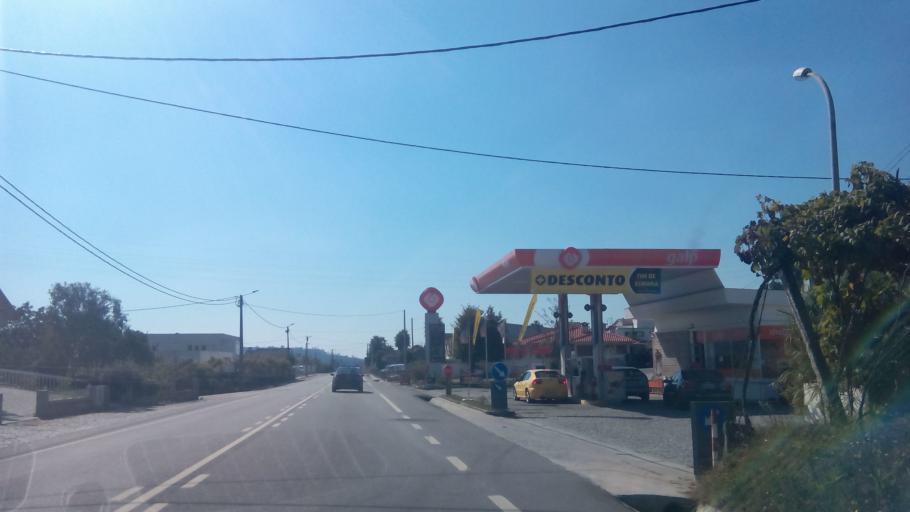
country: PT
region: Porto
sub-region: Lousada
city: Meinedo
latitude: 41.2268
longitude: -8.2336
